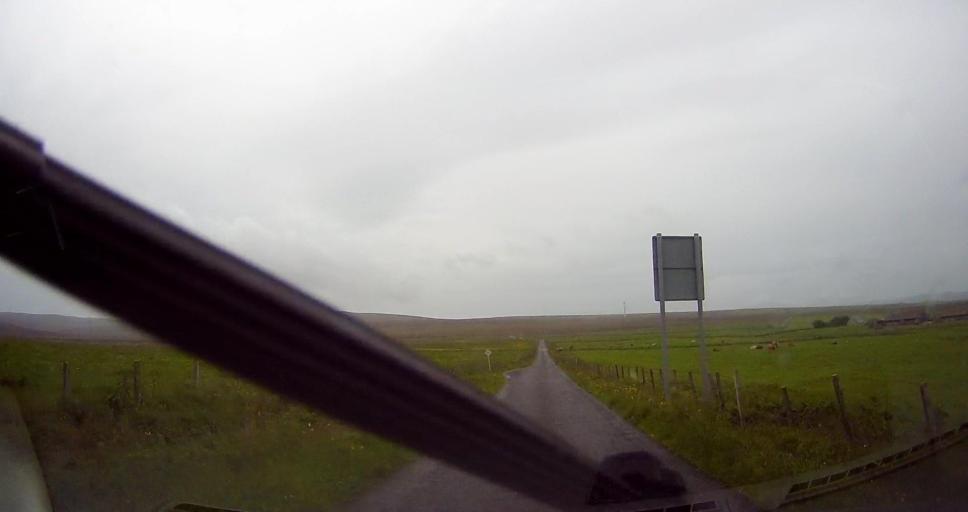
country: GB
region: Scotland
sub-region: Orkney Islands
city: Stromness
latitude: 59.0924
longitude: -3.1827
